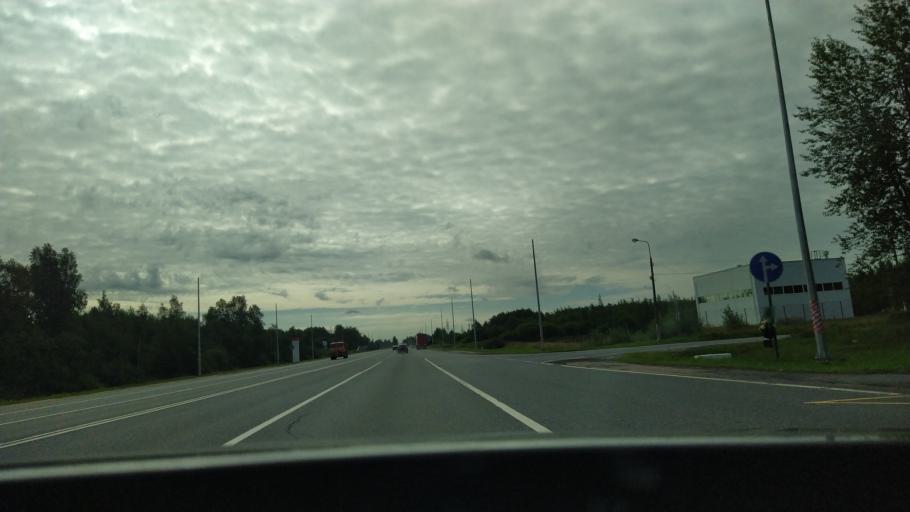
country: RU
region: Leningrad
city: Tosno
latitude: 59.5718
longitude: 30.8208
